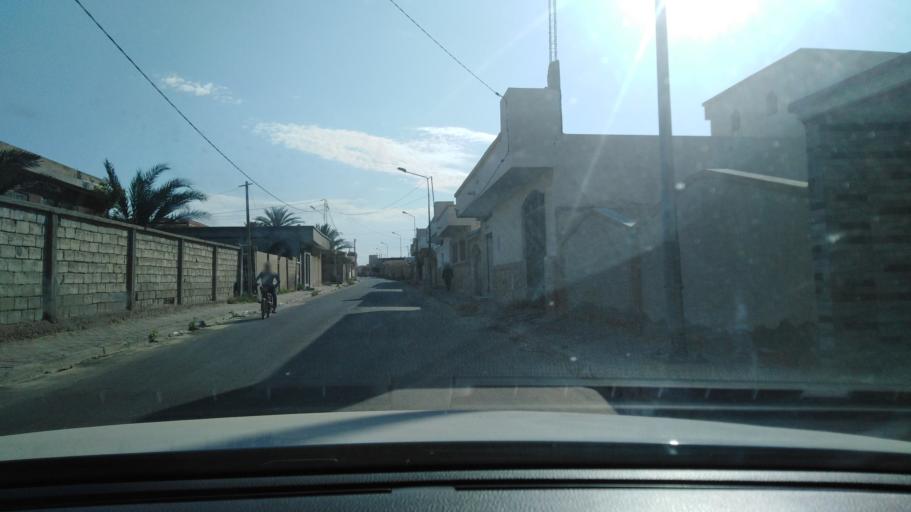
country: TN
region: Qabis
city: Gabes
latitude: 33.9417
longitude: 10.0756
